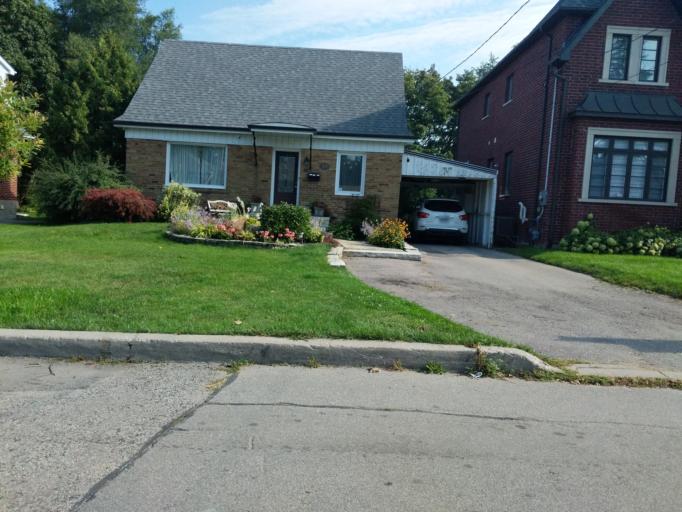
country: CA
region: Ontario
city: Toronto
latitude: 43.7203
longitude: -79.4392
